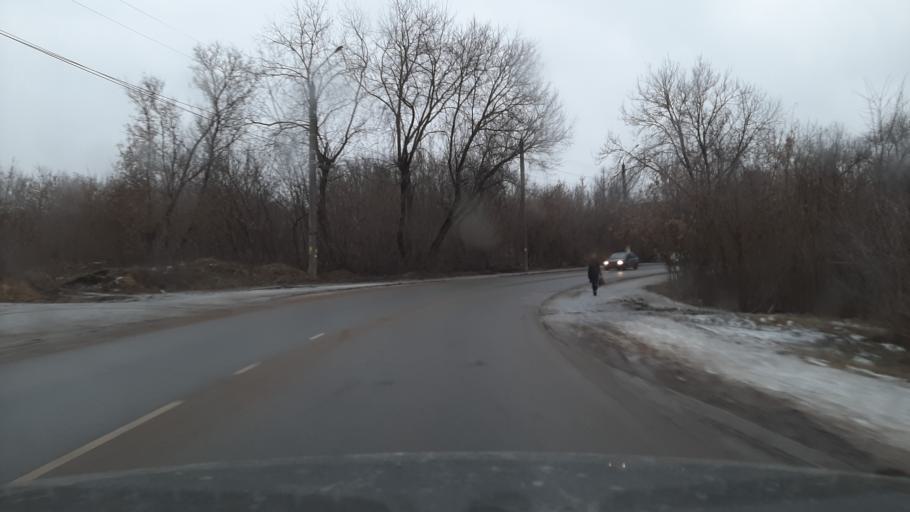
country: RU
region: Ivanovo
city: Shuya
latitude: 56.8569
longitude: 41.3604
